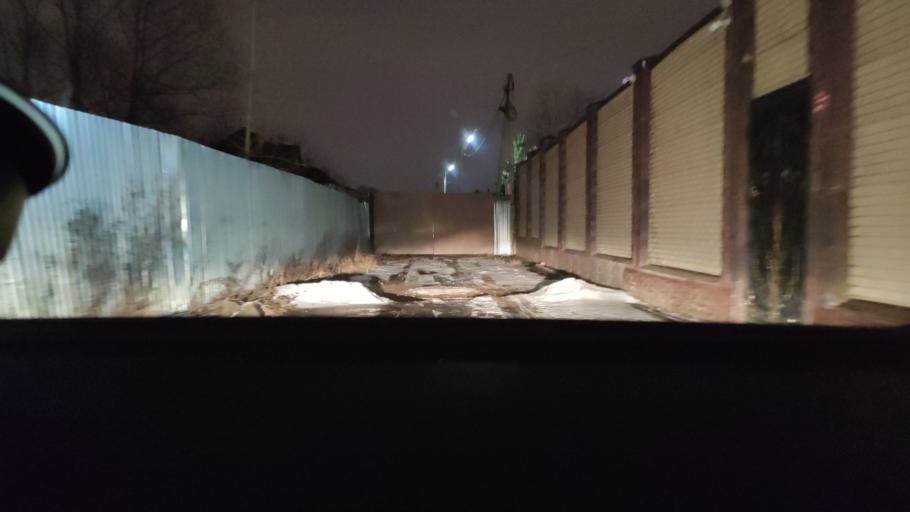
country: RU
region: Moskovskaya
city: Mosrentgen
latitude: 55.6312
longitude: 37.4431
